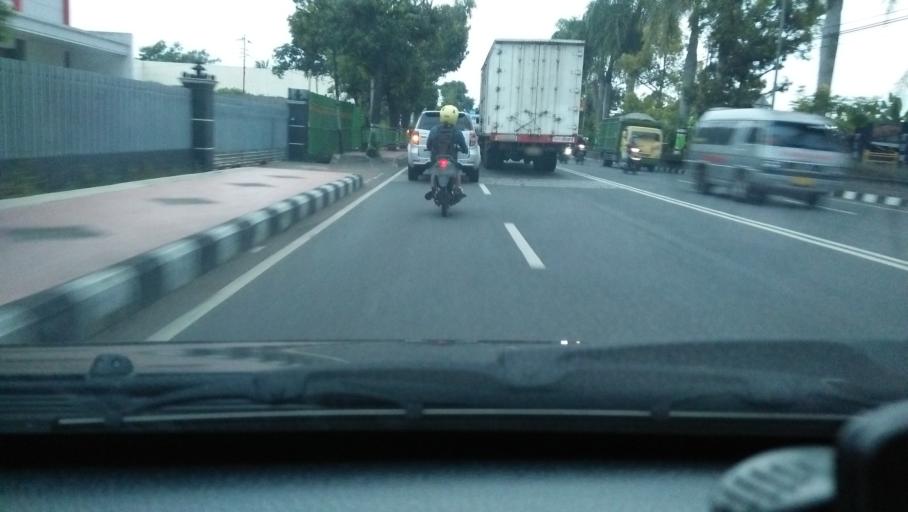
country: ID
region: Central Java
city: Magelang
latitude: -7.4362
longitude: 110.2278
